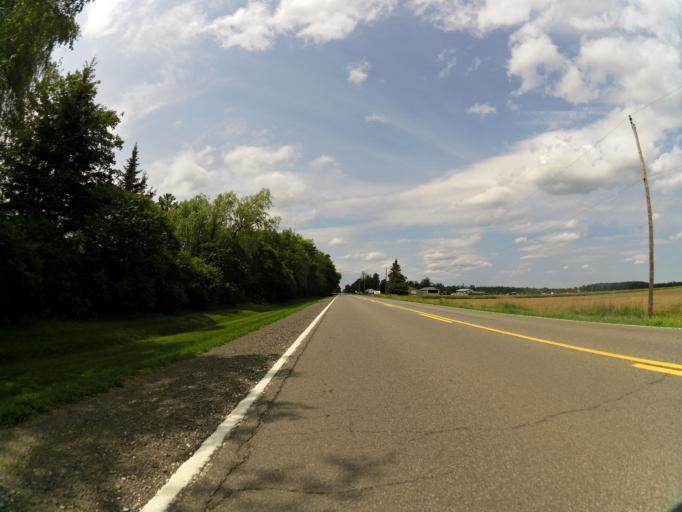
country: CA
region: Ontario
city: Ottawa
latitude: 45.1956
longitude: -75.5889
